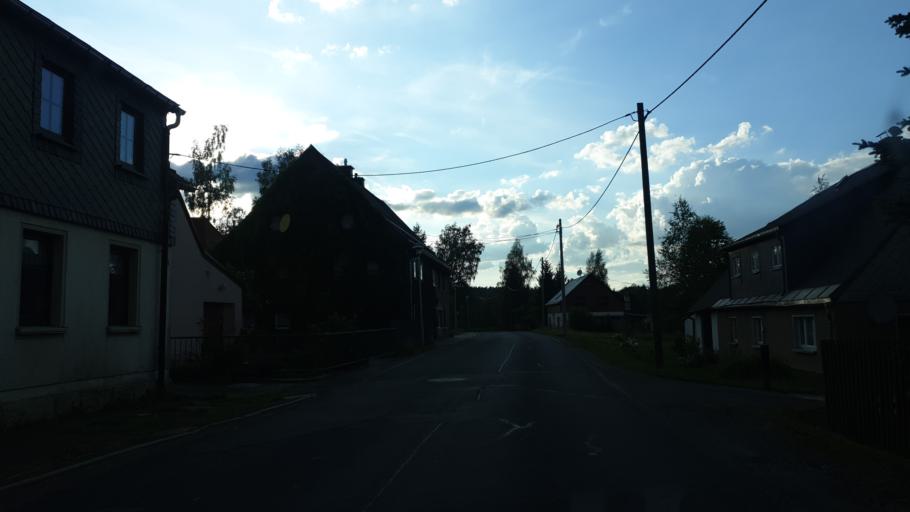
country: DE
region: Saxony
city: Hammerbrucke
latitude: 50.4345
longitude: 12.4184
